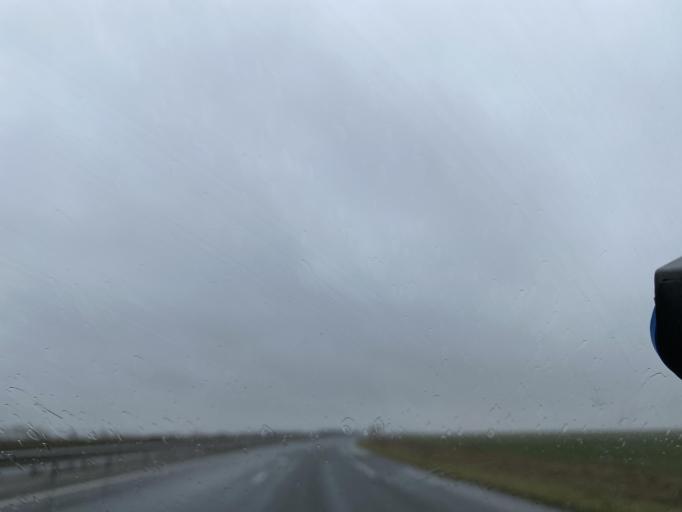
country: FR
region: Centre
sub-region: Departement d'Eure-et-Loir
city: Bailleau-l'Eveque
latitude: 48.5516
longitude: 1.4471
